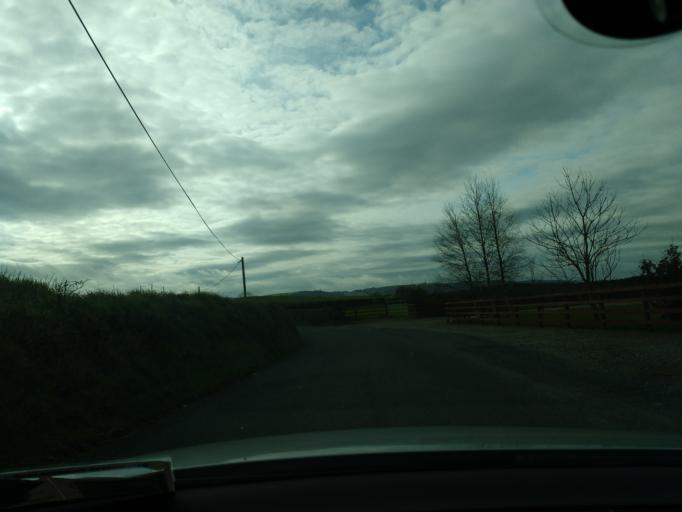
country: IE
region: Leinster
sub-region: Laois
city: Rathdowney
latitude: 52.6845
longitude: -7.6133
